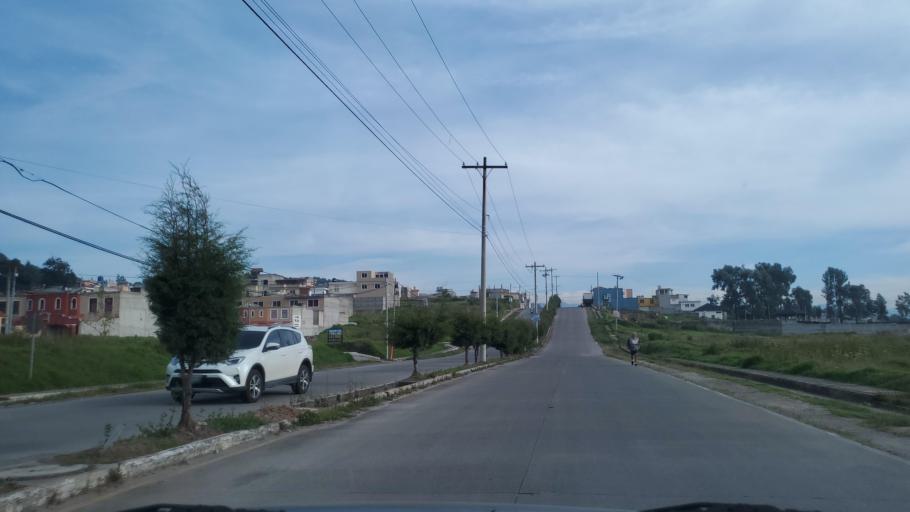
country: GT
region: Quetzaltenango
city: Quetzaltenango
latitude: 14.8320
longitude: -91.5496
